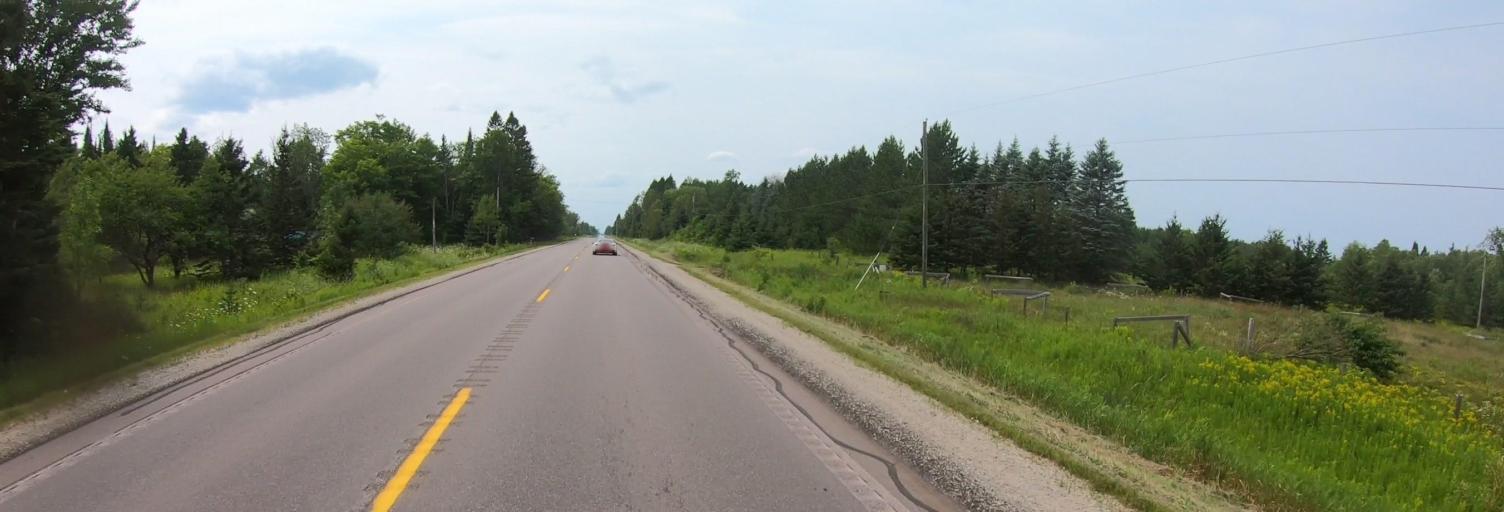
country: US
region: Michigan
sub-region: Marquette County
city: K. I. Sawyer Air Force Base
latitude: 46.3475
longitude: -87.1500
